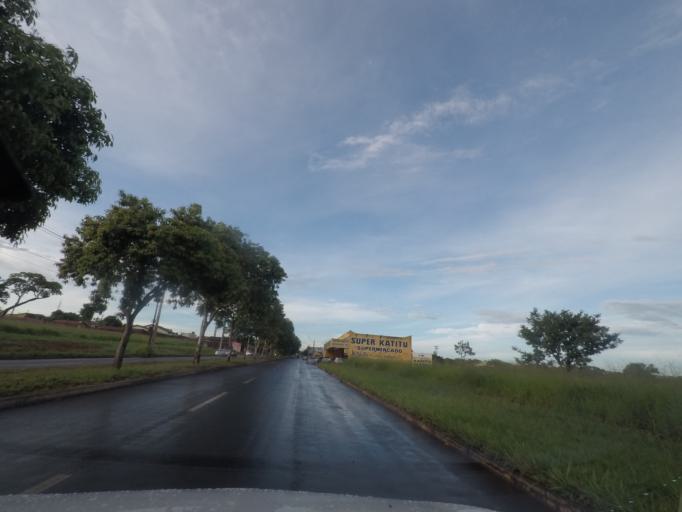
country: BR
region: Goias
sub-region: Goiania
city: Goiania
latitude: -16.7333
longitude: -49.3667
